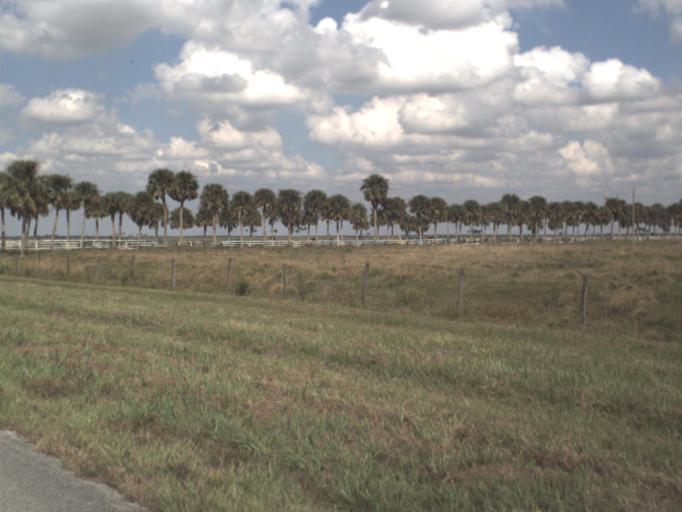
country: US
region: Florida
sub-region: Okeechobee County
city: Okeechobee
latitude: 27.3281
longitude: -80.9252
